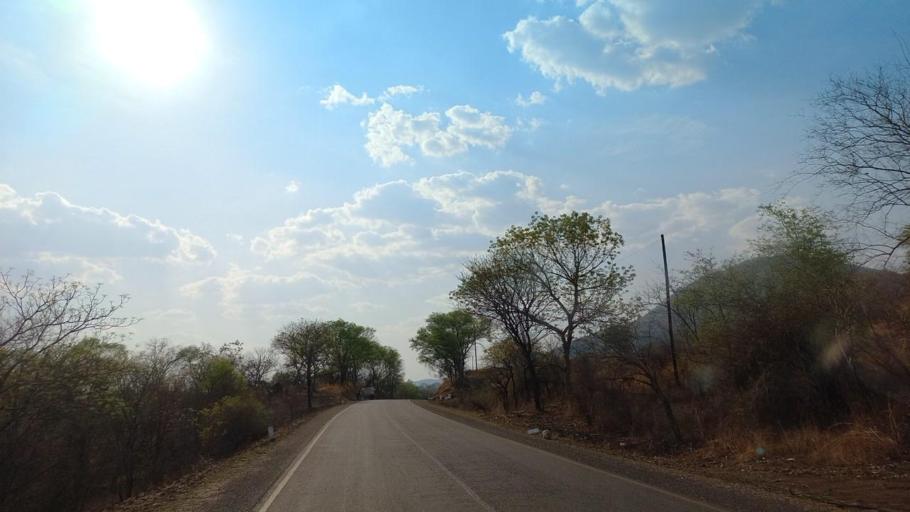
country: ZM
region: Lusaka
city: Luangwa
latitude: -14.9836
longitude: 30.1554
